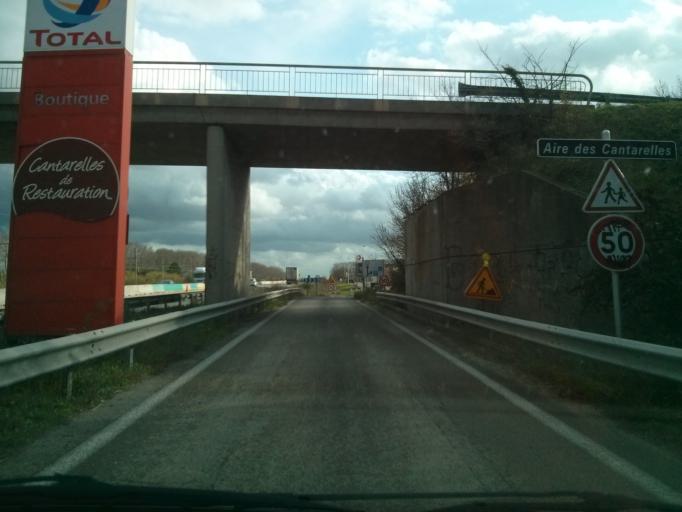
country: FR
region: Provence-Alpes-Cote d'Azur
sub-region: Departement des Bouches-du-Rhone
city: Arles
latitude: 43.6522
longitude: 4.6681
